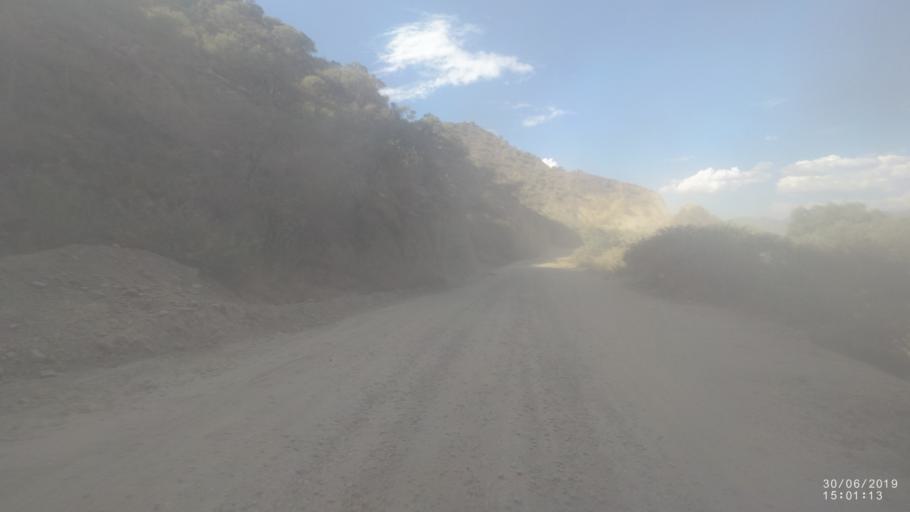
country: BO
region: Cochabamba
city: Irpa Irpa
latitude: -17.7334
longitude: -66.3375
